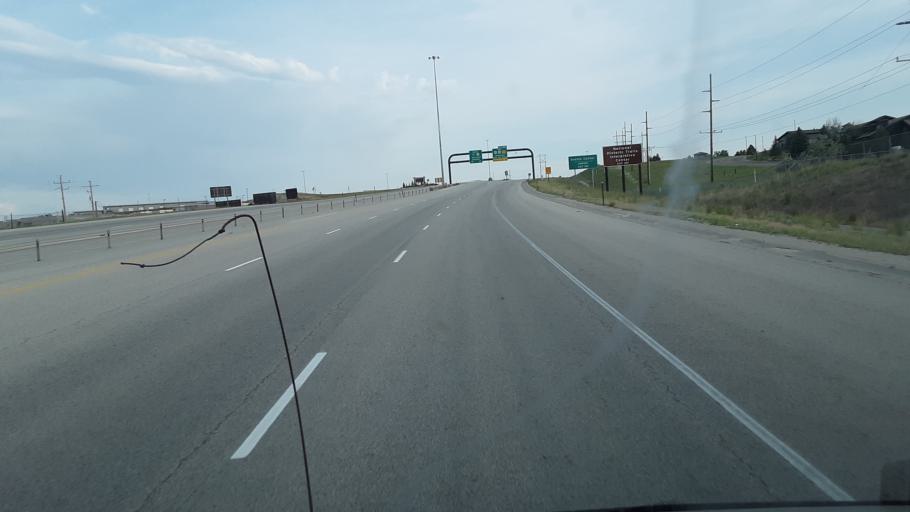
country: US
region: Wyoming
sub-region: Natrona County
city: Casper
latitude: 42.8617
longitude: -106.3393
